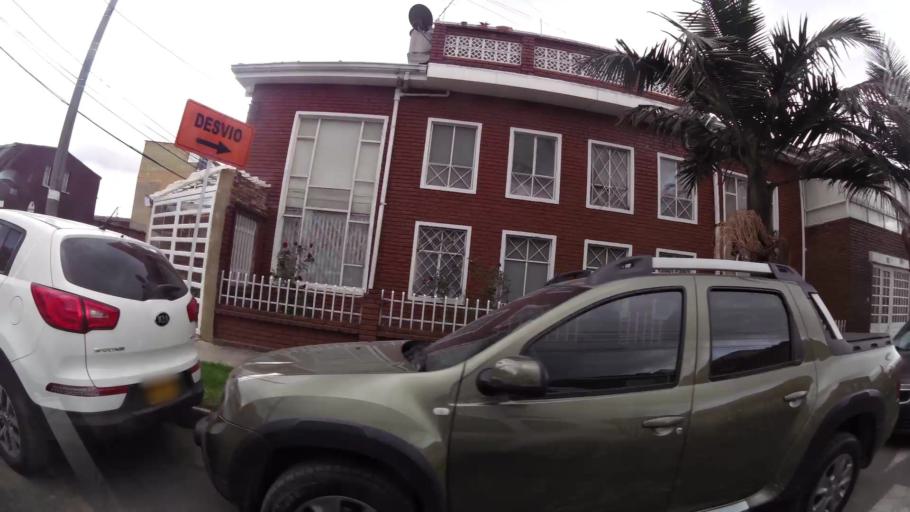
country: CO
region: Bogota D.C.
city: Bogota
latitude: 4.6080
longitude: -74.1153
